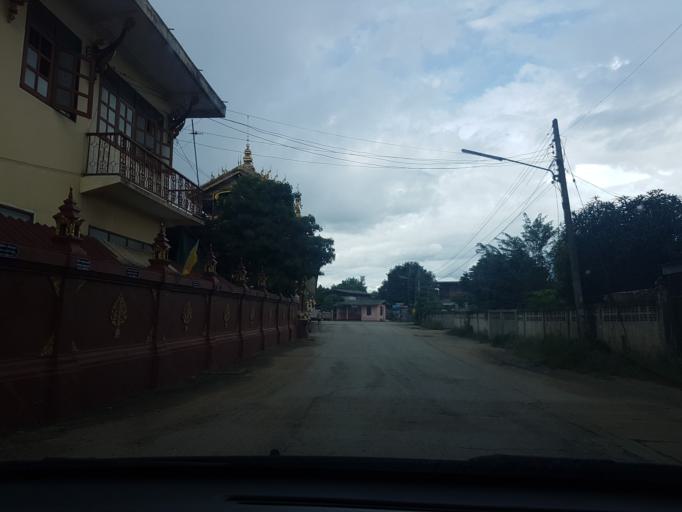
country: TH
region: Lampang
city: Ko Kha
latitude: 18.2343
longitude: 99.4226
